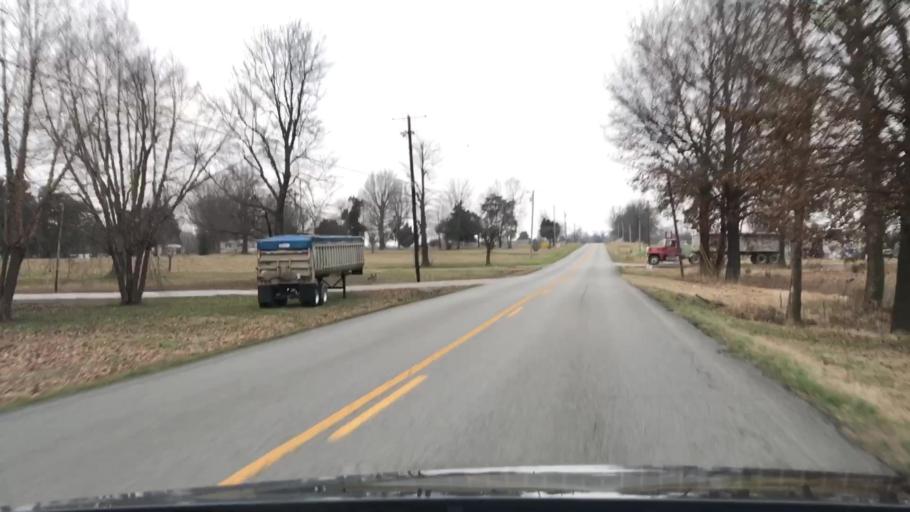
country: US
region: Kentucky
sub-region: Muhlenberg County
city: Morehead
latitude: 37.3914
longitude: -87.2549
